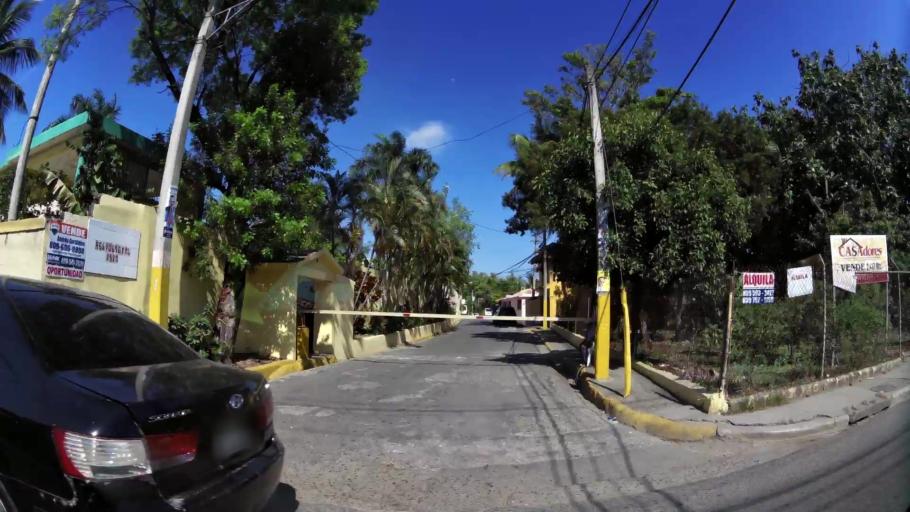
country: DO
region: Santo Domingo
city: Santo Domingo Oeste
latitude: 18.4713
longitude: -69.9993
